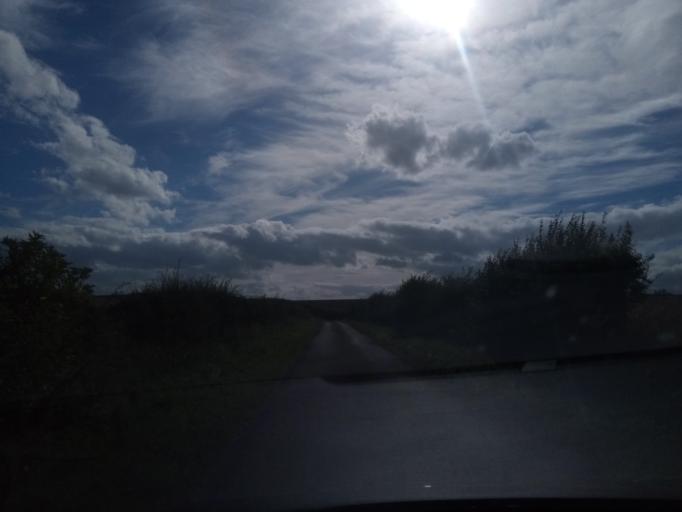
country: GB
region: England
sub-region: Northumberland
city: Kirknewton
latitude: 55.6095
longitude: -2.1778
